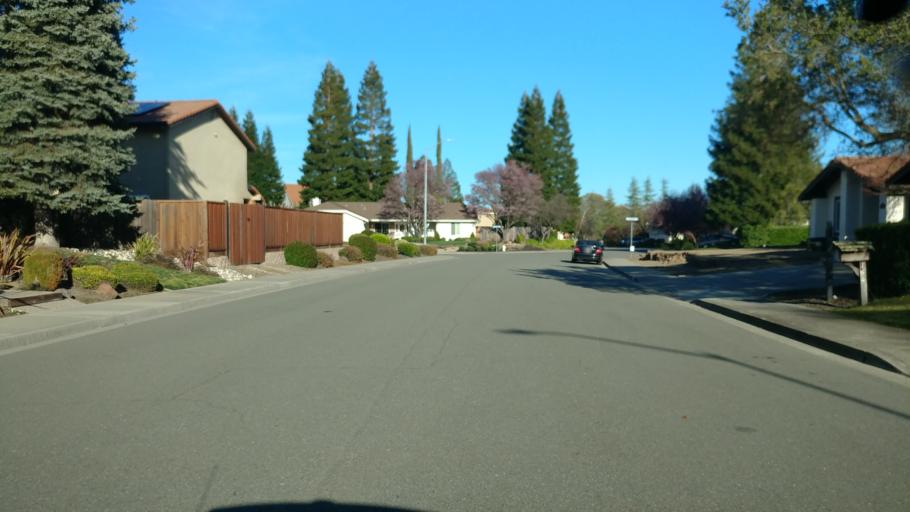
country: US
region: California
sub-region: Contra Costa County
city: San Ramon
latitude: 37.7538
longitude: -121.9704
